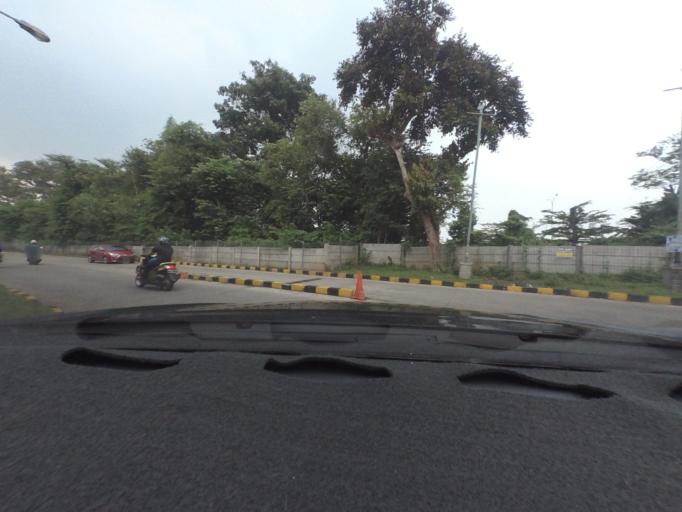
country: ID
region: West Java
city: Bogor
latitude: -6.5971
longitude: 106.8211
